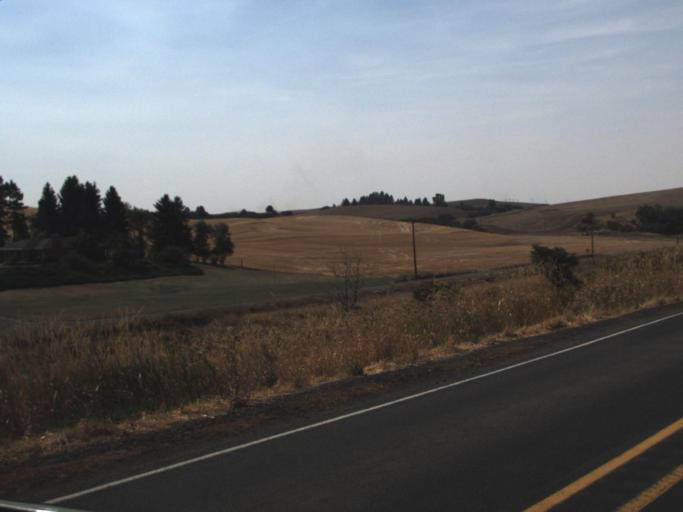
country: US
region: Idaho
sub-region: Benewah County
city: Plummer
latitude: 47.2296
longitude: -117.0869
